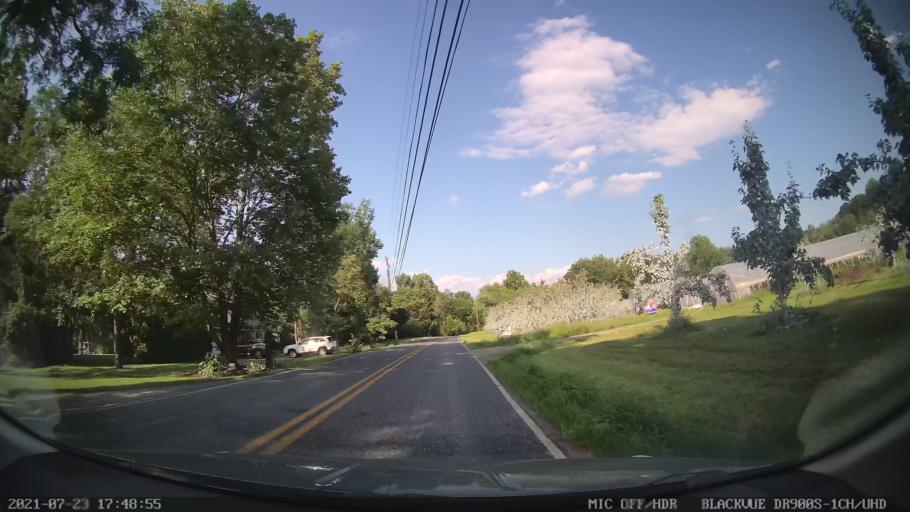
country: US
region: Pennsylvania
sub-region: Berks County
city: Red Lion
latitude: 40.4915
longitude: -75.6139
